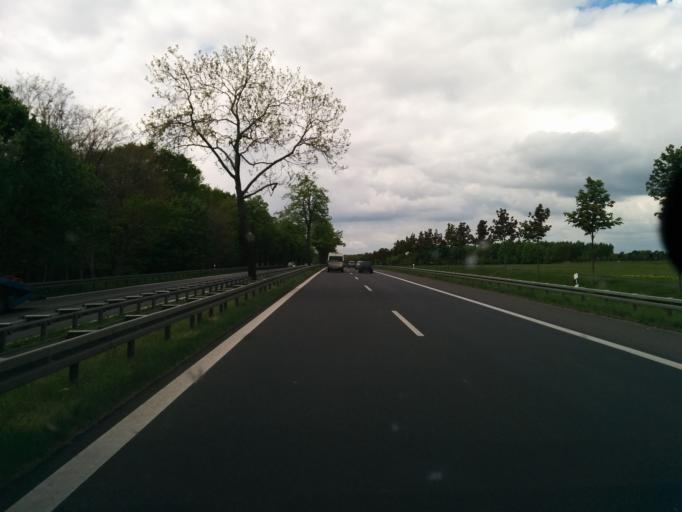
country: DE
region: Brandenburg
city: Dallgow-Doeberitz
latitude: 52.5339
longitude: 13.0317
